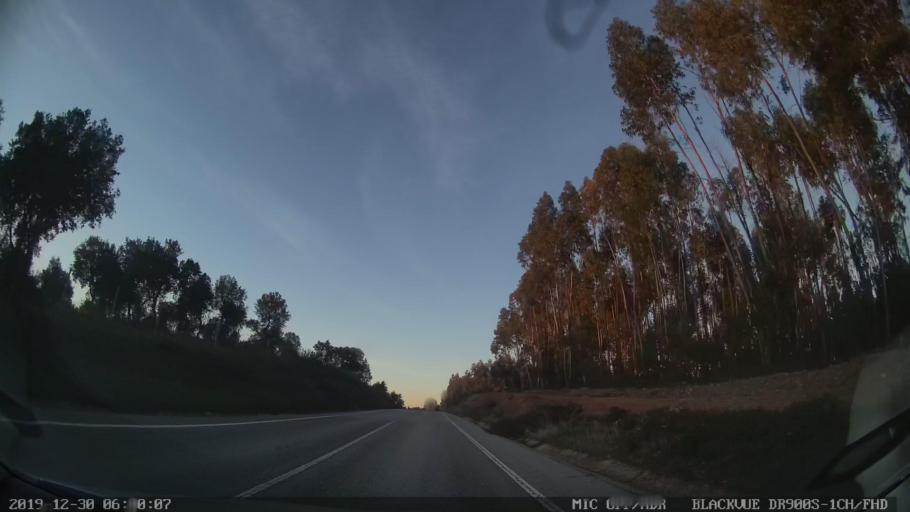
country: PT
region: Castelo Branco
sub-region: Idanha-A-Nova
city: Idanha-a-Nova
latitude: 40.0496
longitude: -7.2442
